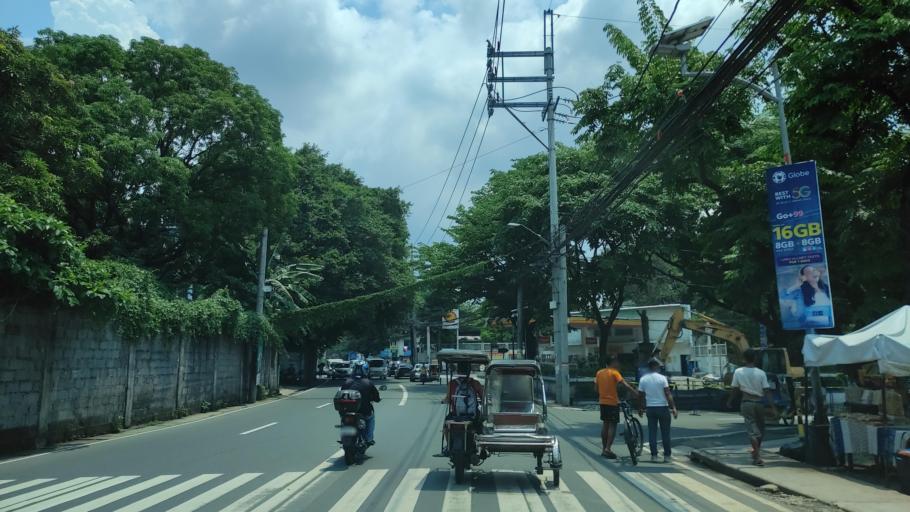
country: PH
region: Calabarzon
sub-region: Province of Rizal
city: Taytay
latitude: 14.5875
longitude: 121.1708
